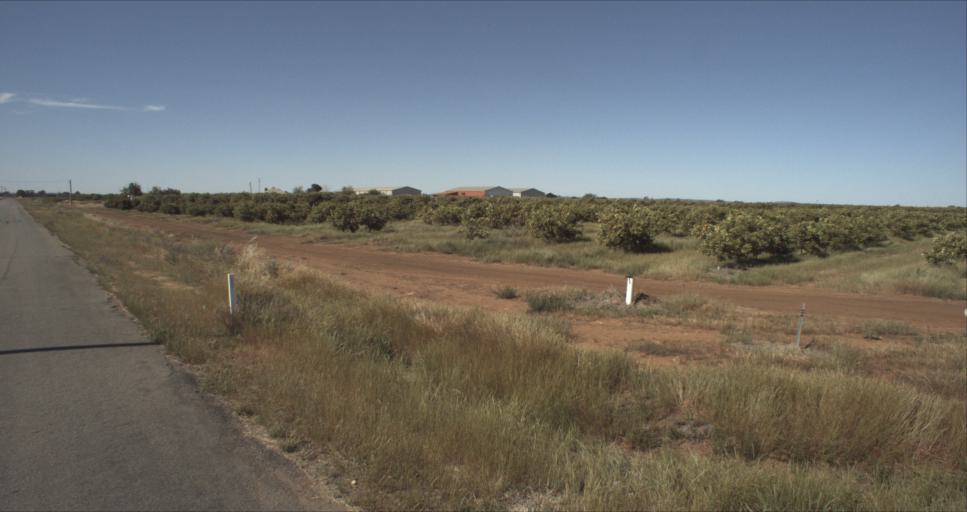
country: AU
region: New South Wales
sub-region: Leeton
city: Leeton
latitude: -34.5878
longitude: 146.3786
